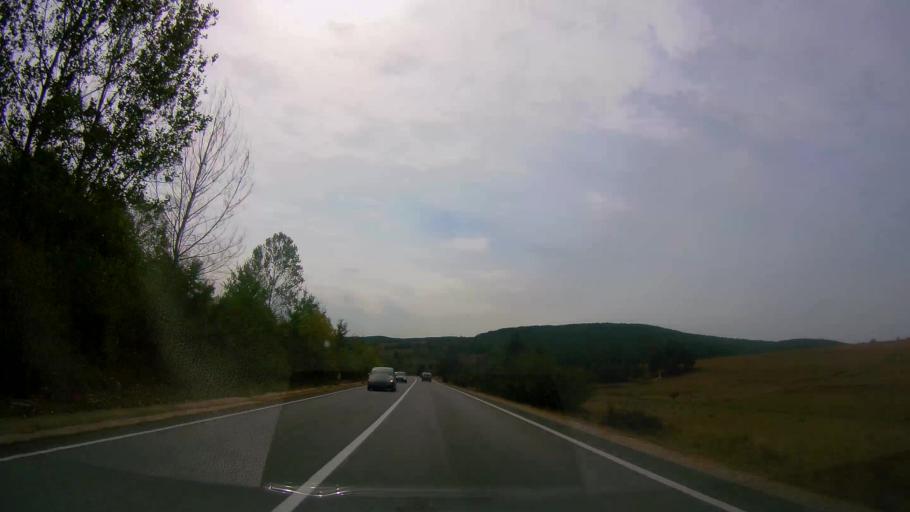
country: RO
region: Salaj
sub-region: Comuna Romanasi
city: Romanasi
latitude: 47.0618
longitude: 23.2130
